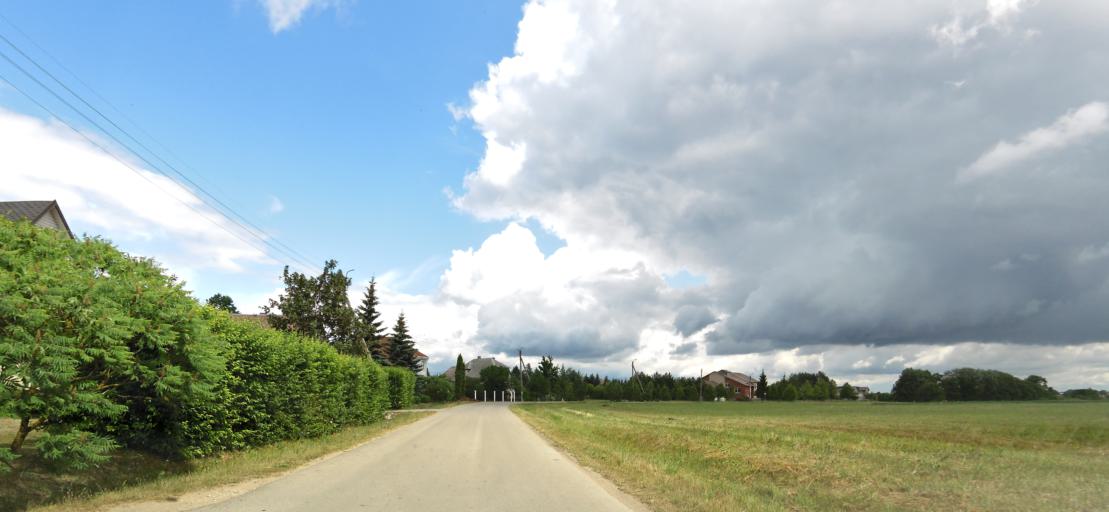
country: LT
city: Kupiskis
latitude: 55.8439
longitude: 24.9508
